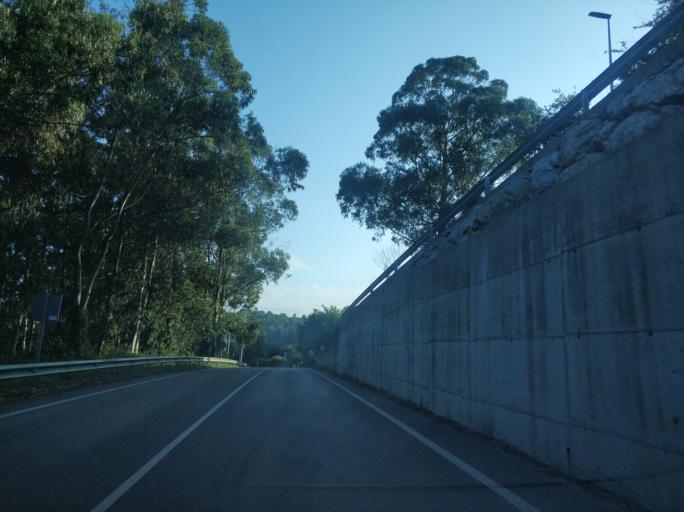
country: ES
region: Cantabria
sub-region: Provincia de Cantabria
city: Camargo
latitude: 43.3986
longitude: -3.9422
